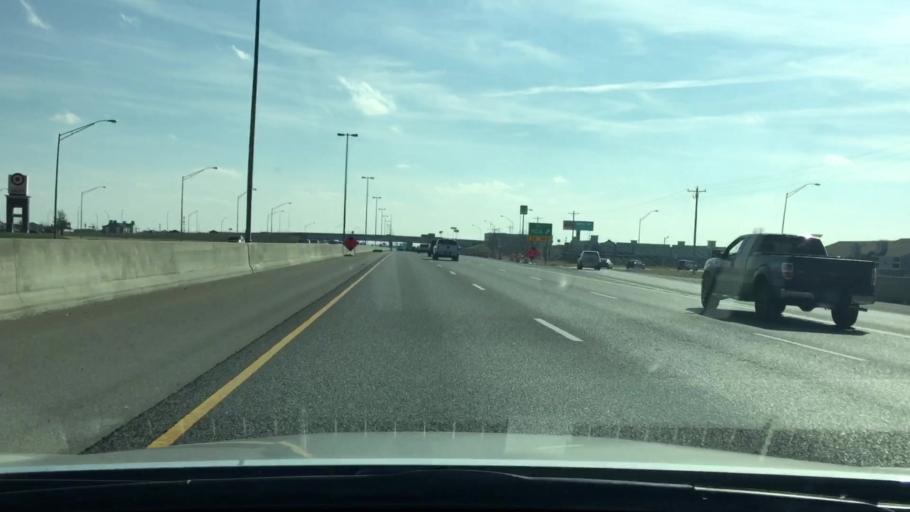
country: US
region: Oklahoma
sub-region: Cleveland County
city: Norman
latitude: 35.2375
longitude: -97.4856
